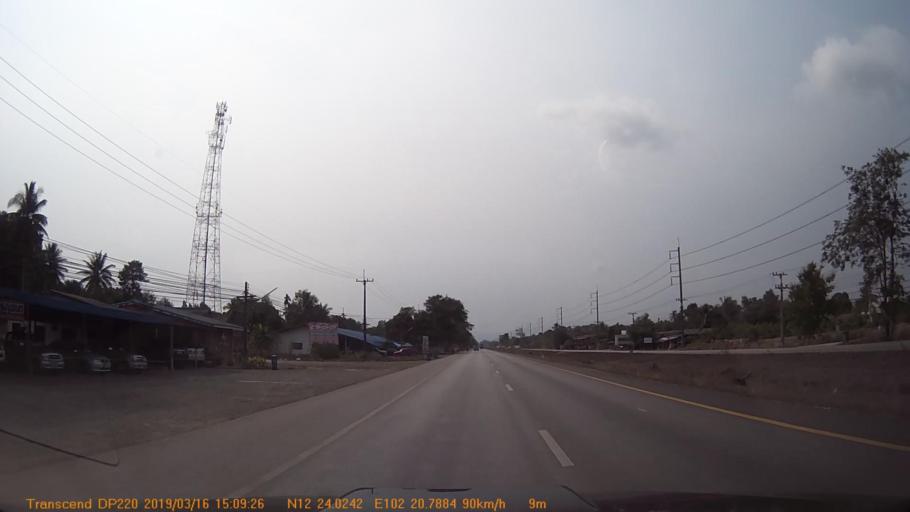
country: TH
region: Trat
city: Khao Saming
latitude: 12.4006
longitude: 102.3463
